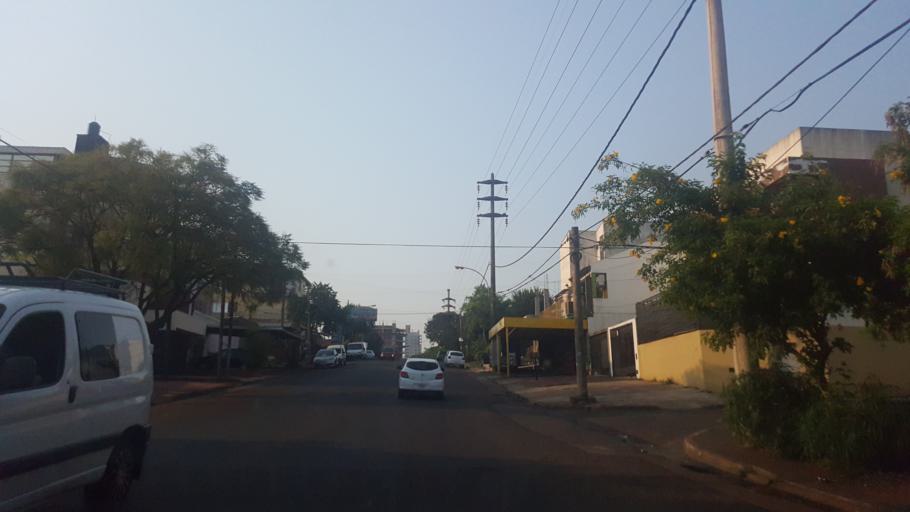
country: AR
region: Misiones
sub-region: Departamento de Capital
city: Posadas
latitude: -27.3777
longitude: -55.8914
